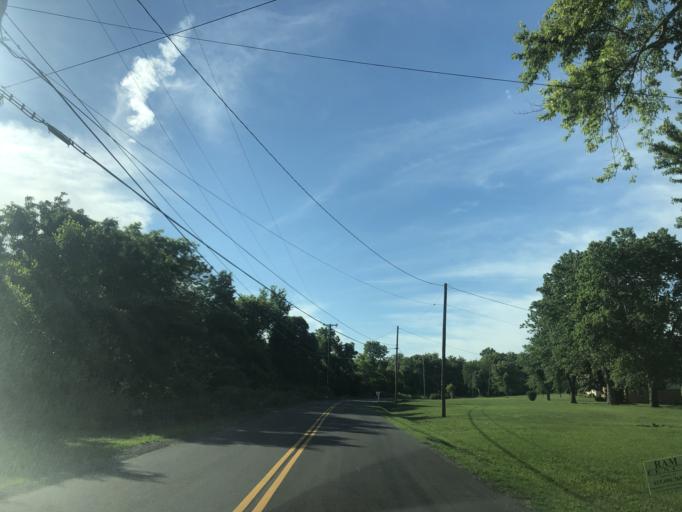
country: US
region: Tennessee
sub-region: Davidson County
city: Nashville
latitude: 36.2180
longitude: -86.8492
